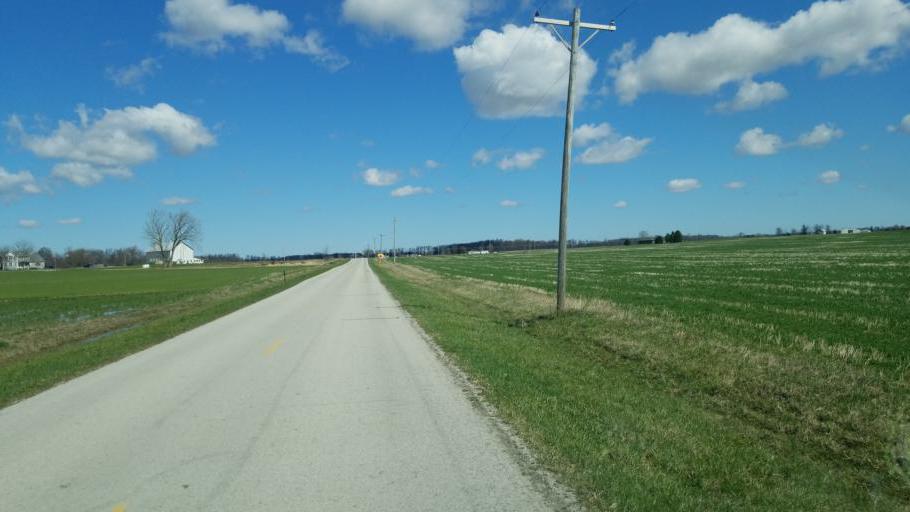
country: US
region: Ohio
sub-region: Sandusky County
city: Mount Carmel
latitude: 41.2030
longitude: -82.9373
